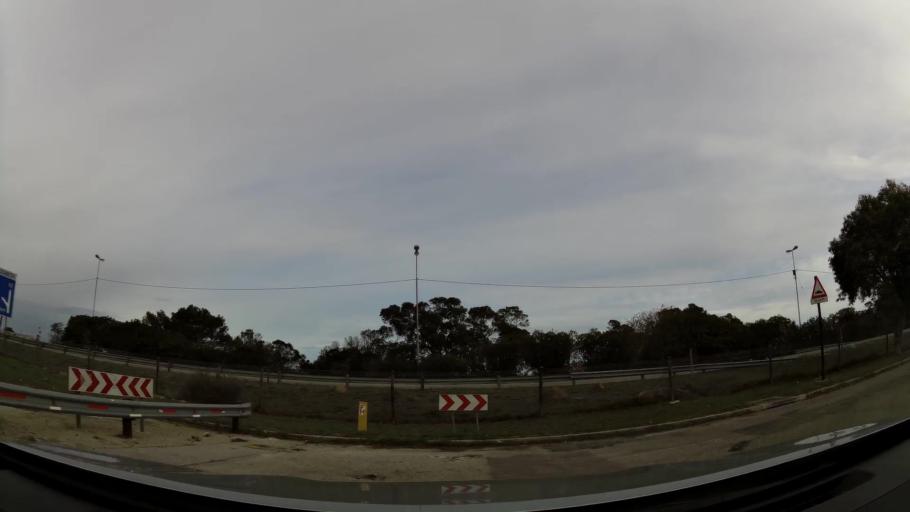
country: ZA
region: Eastern Cape
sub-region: Nelson Mandela Bay Metropolitan Municipality
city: Port Elizabeth
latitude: -33.9453
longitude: 25.4956
